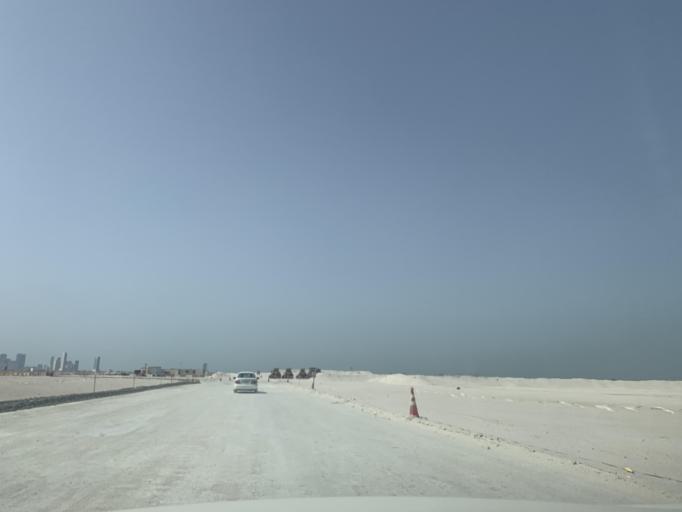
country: BH
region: Northern
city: Sitrah
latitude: 26.1667
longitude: 50.6362
